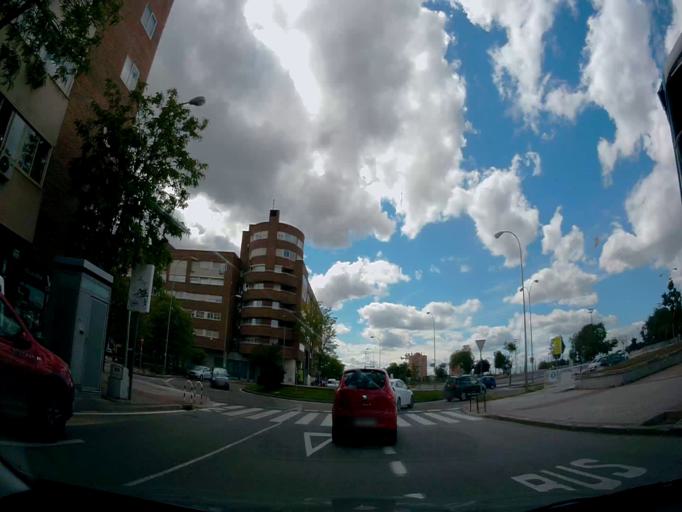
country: ES
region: Madrid
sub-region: Provincia de Madrid
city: Vicalvaro
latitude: 40.4038
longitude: -3.6196
